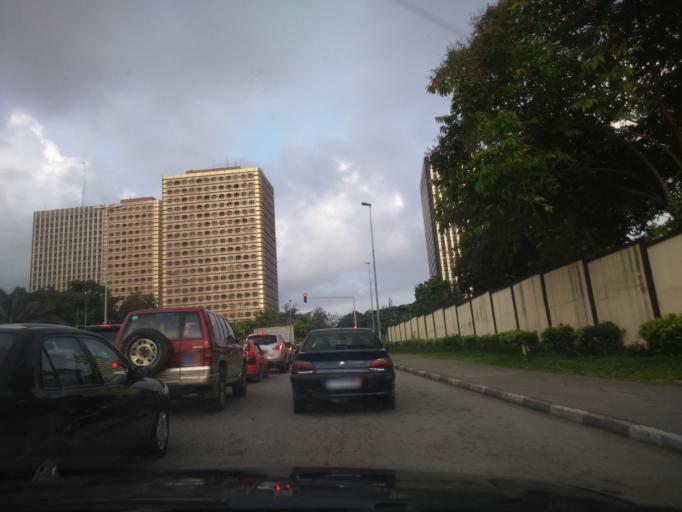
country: CI
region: Lagunes
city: Abidjan
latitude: 5.3347
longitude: -4.0209
